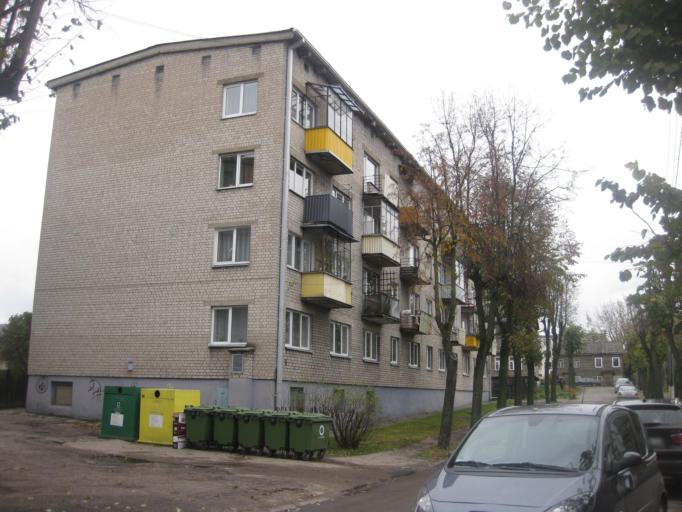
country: LT
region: Kauno apskritis
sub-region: Kaunas
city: Kaunas
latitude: 54.9066
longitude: 23.9170
